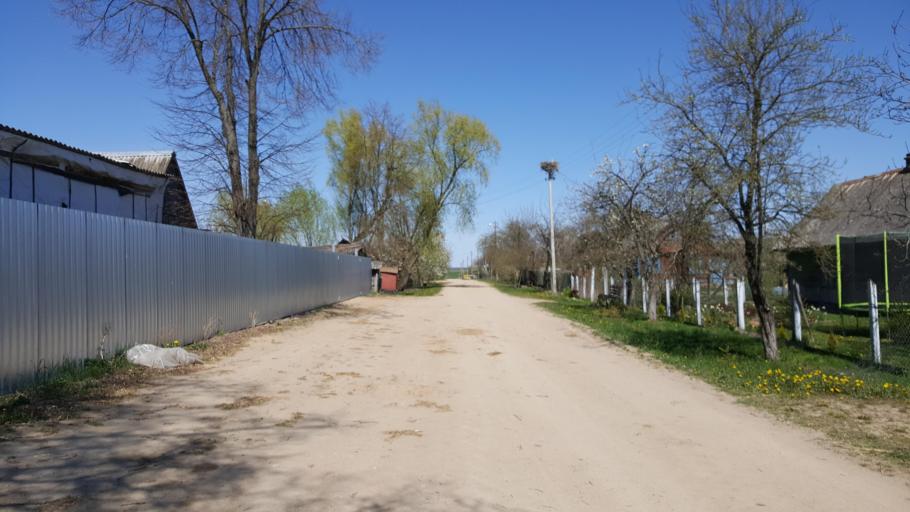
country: BY
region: Brest
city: Vysokaye
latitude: 52.3453
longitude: 23.5282
